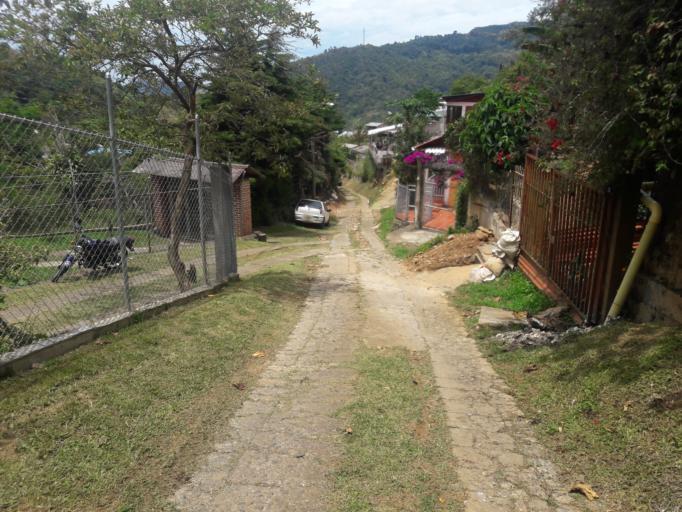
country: CO
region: Valle del Cauca
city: Cali
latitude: 3.4698
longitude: -76.6306
